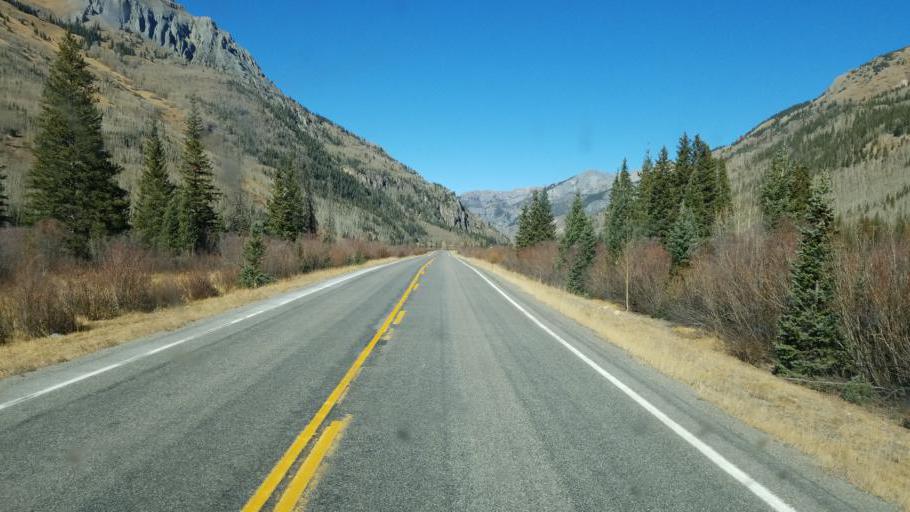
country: US
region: Colorado
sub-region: Ouray County
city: Ouray
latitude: 37.9434
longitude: -107.6683
